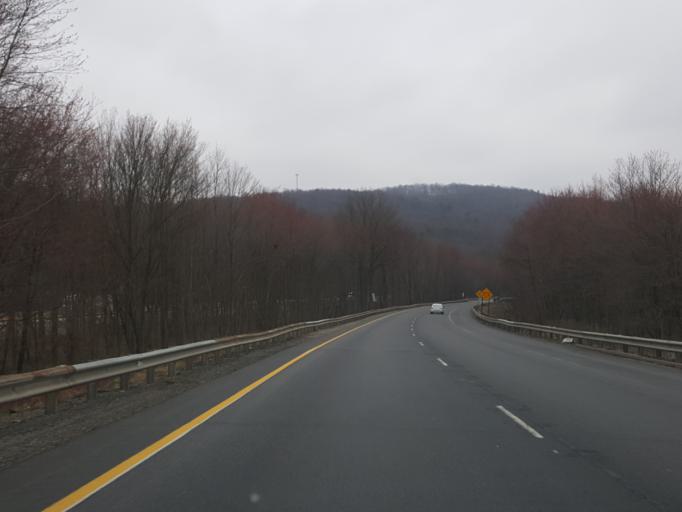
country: US
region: Pennsylvania
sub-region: Schuylkill County
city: Pine Grove
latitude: 40.5292
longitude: -76.4315
